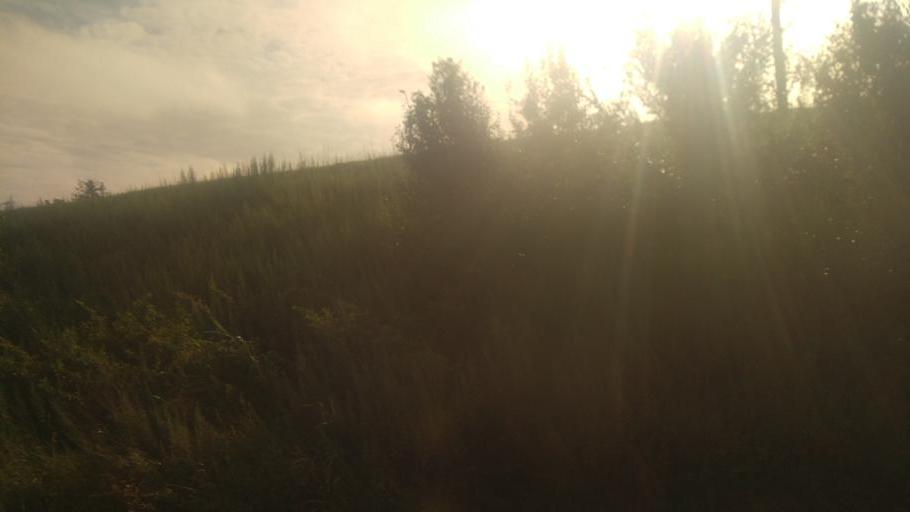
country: US
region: North Carolina
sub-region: Wake County
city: Raleigh
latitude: 35.7671
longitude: -78.6396
